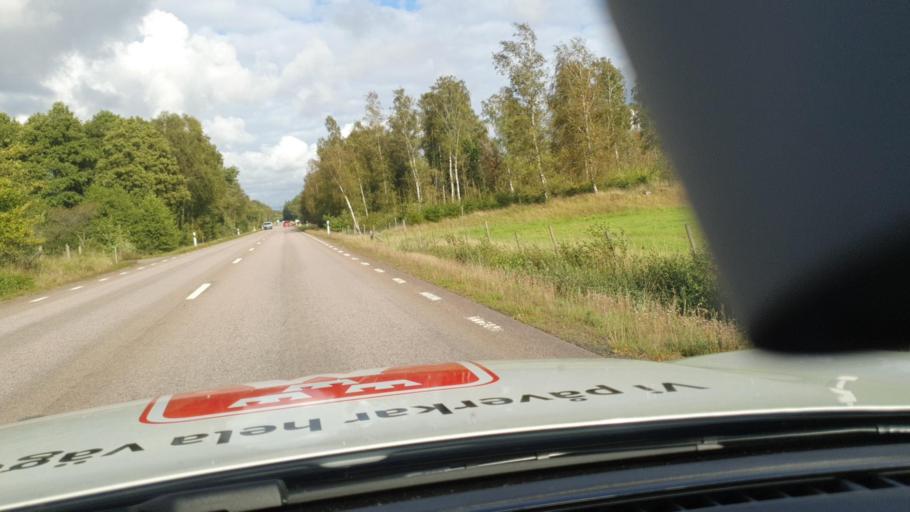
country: SE
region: Skane
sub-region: Angelholms Kommun
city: Munka-Ljungby
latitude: 56.2714
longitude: 13.0069
